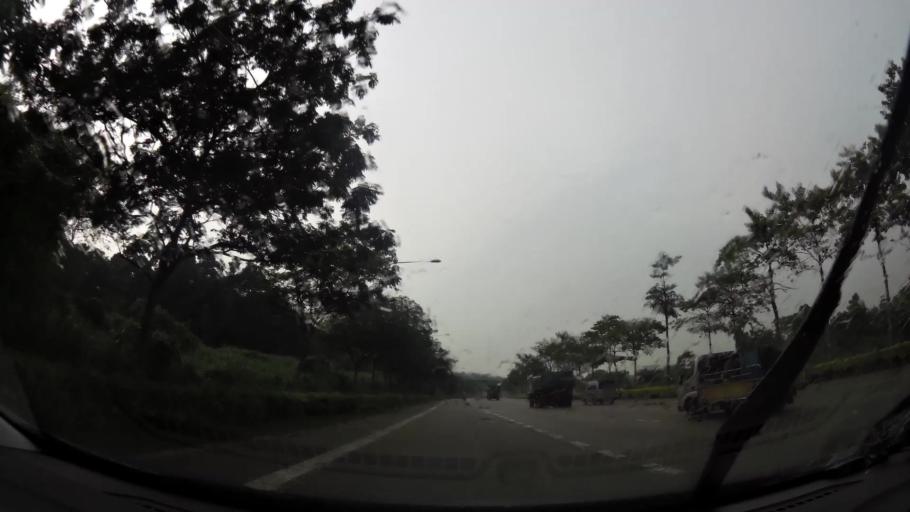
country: MY
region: Johor
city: Kampung Pasir Gudang Baru
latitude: 1.3930
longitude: 103.8295
